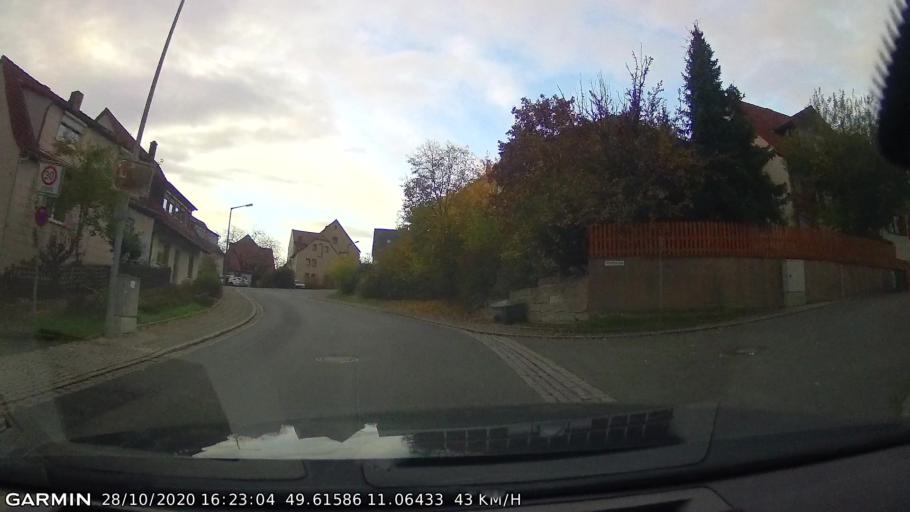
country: DE
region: Bavaria
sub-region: Regierungsbezirk Mittelfranken
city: Marloffstein
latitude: 49.6160
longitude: 11.0645
